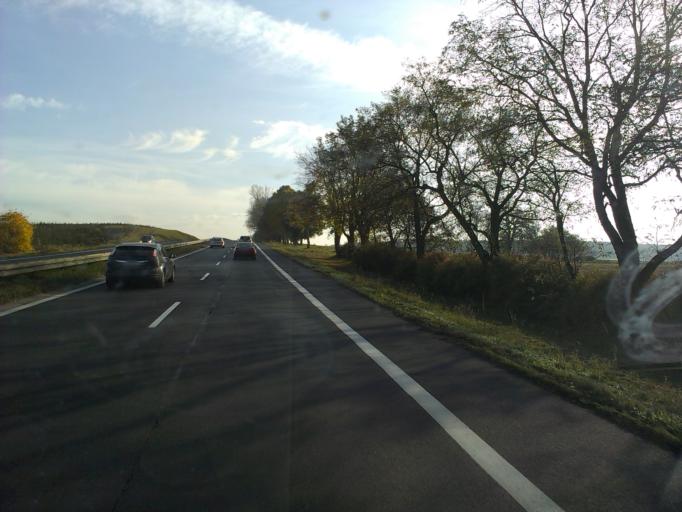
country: PL
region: Lower Silesian Voivodeship
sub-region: Powiat polkowicki
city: Polkowice
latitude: 51.5328
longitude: 16.0535
